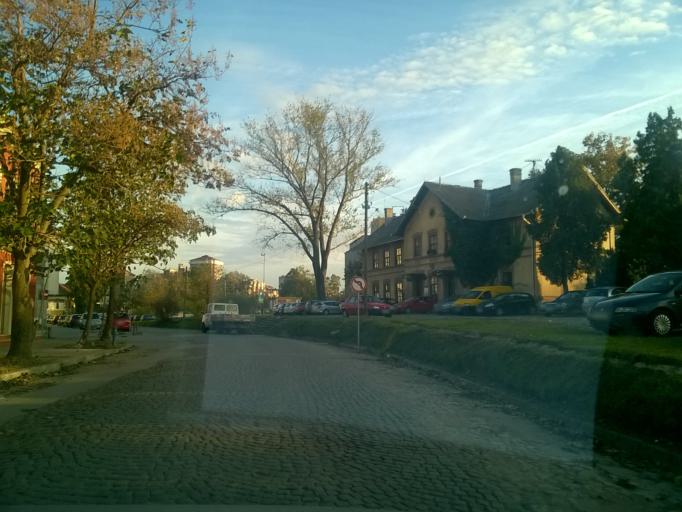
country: RS
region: Autonomna Pokrajina Vojvodina
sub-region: Juznobanatski Okrug
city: Pancevo
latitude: 44.8697
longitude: 20.6369
